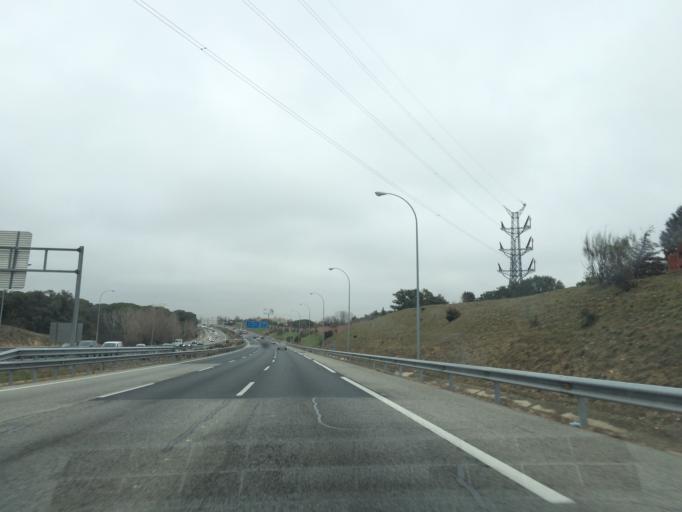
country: ES
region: Madrid
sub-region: Provincia de Madrid
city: Pozuelo de Alarcon
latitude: 40.4461
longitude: -3.8254
